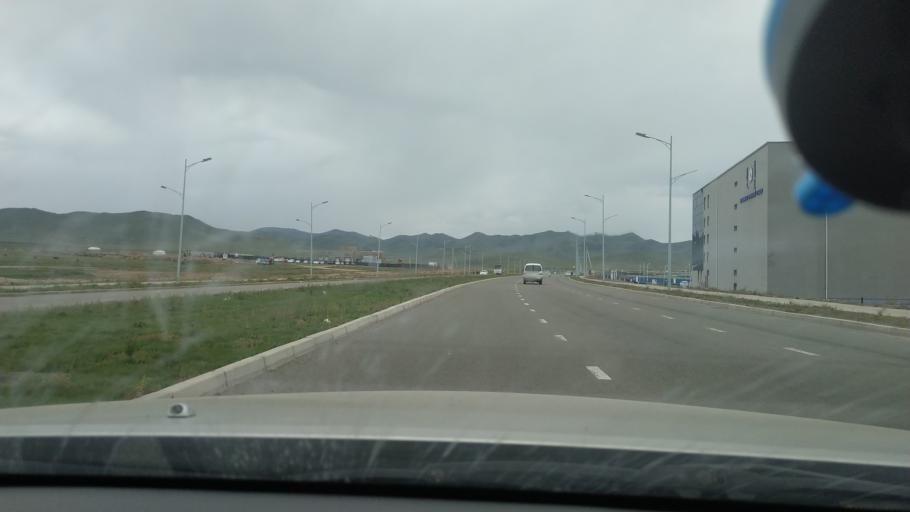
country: MN
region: Ulaanbaatar
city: Ulaanbaatar
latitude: 47.8421
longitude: 106.7909
